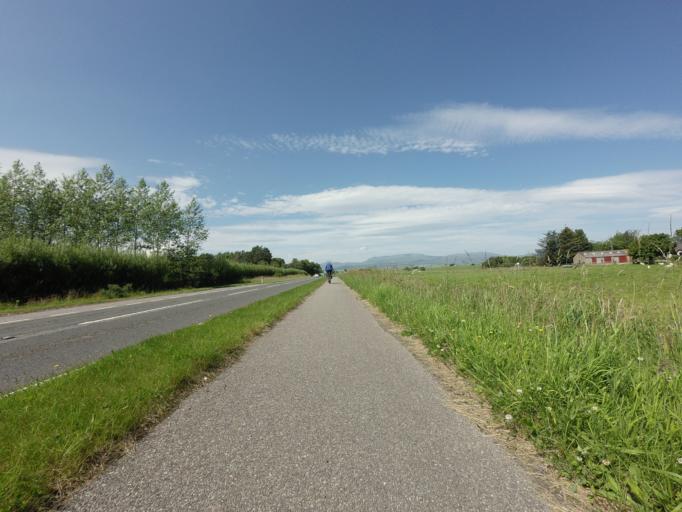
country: GB
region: Scotland
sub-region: Highland
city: Conon Bridge
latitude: 57.5469
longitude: -4.3879
